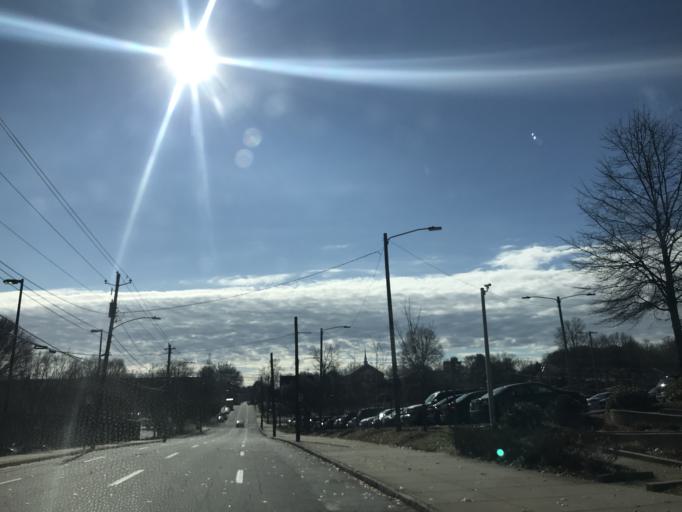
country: US
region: Georgia
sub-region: Fulton County
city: Atlanta
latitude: 33.7433
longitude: -84.3945
